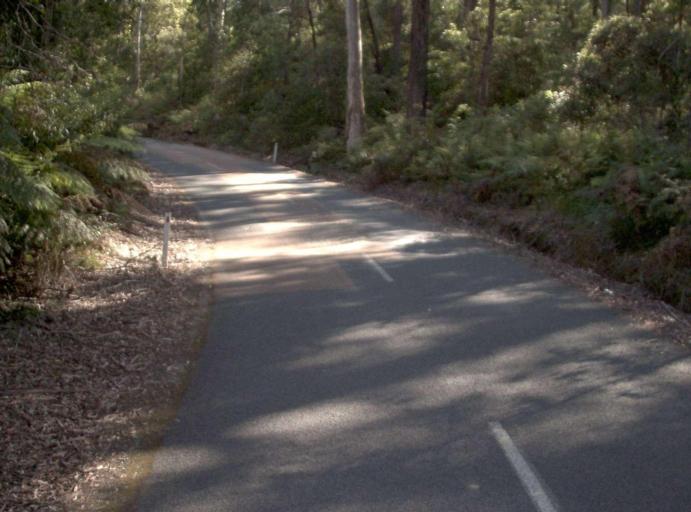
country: AU
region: Victoria
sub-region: East Gippsland
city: Lakes Entrance
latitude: -37.4467
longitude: 148.5823
